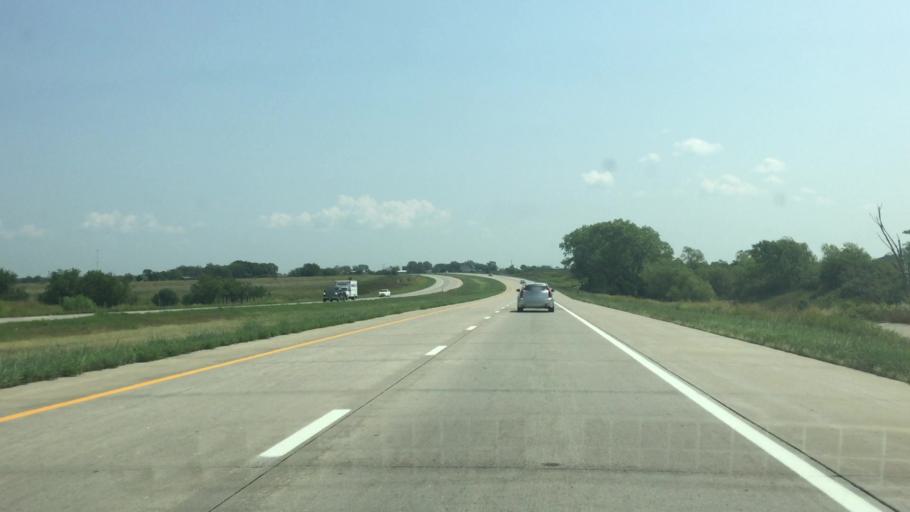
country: US
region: Kansas
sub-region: Franklin County
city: Ottawa
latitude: 38.5010
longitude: -95.4417
